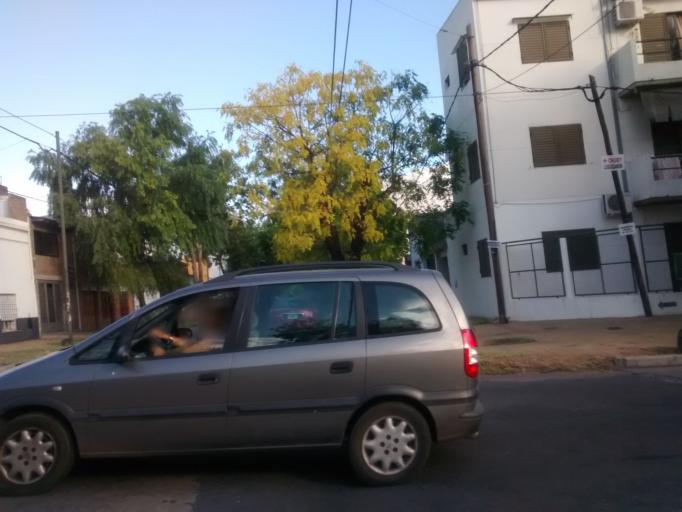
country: AR
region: Buenos Aires
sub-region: Partido de La Plata
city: La Plata
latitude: -34.9124
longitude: -57.9737
